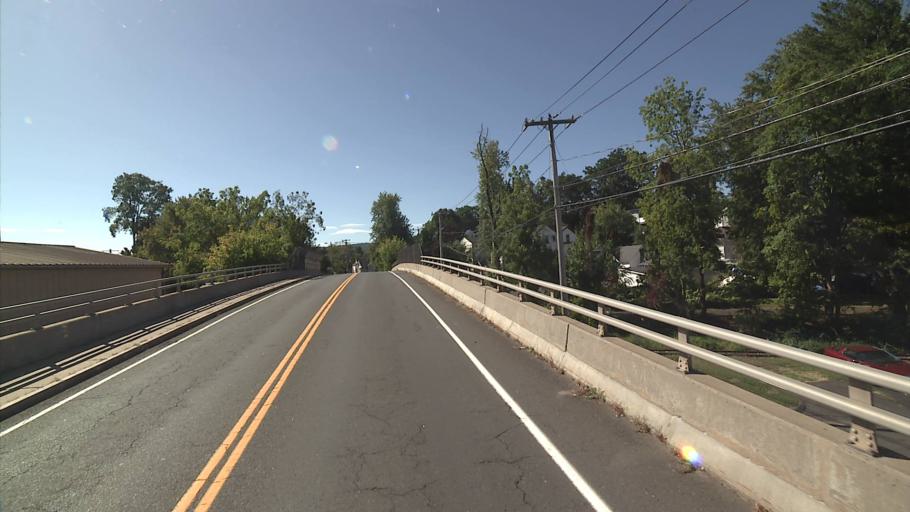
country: US
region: Connecticut
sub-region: Hartford County
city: Bristol
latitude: 41.6859
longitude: -72.9425
